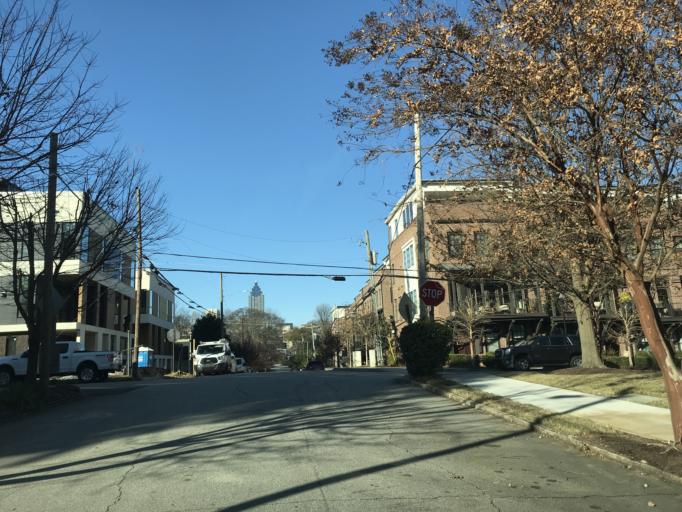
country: US
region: Georgia
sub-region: Fulton County
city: Atlanta
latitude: 33.7632
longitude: -84.3663
